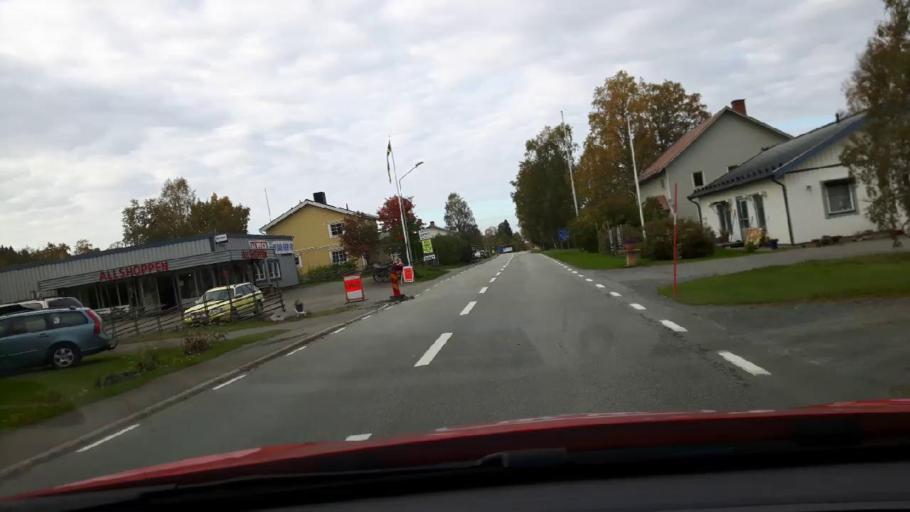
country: SE
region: Jaemtland
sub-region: Krokoms Kommun
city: Krokom
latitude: 63.1762
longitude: 14.0935
